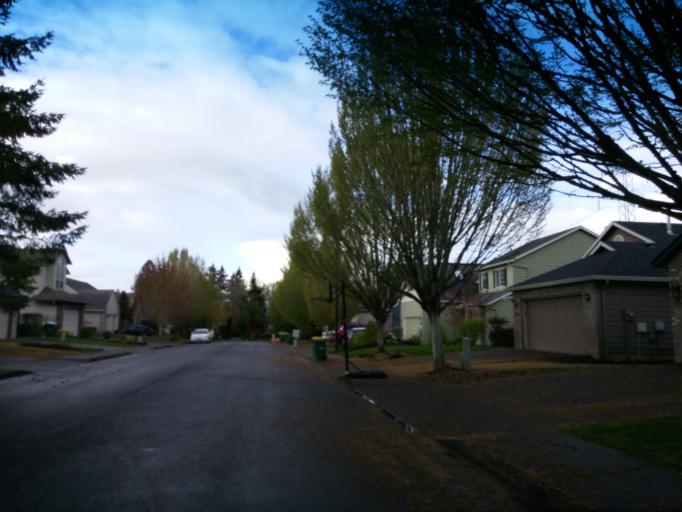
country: US
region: Oregon
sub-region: Washington County
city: Aloha
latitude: 45.5136
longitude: -122.8473
